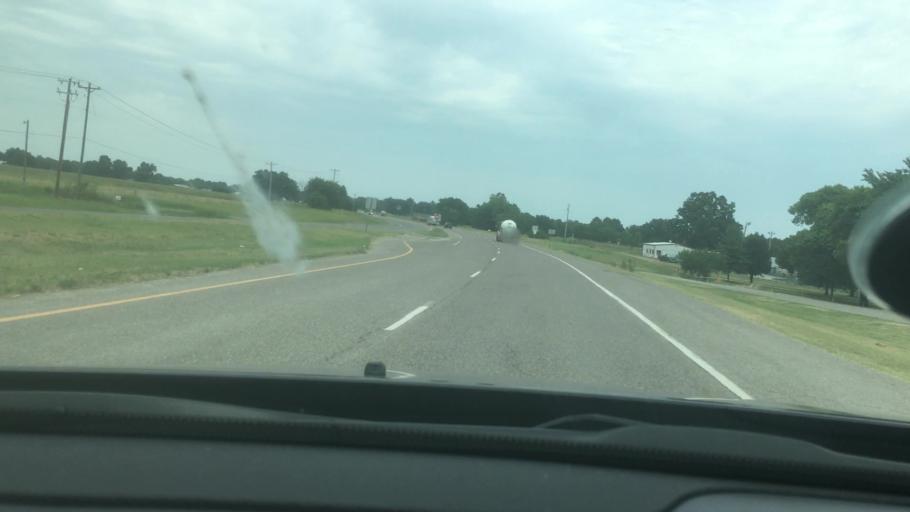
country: US
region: Oklahoma
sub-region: Murray County
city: Davis
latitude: 34.4619
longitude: -97.1307
